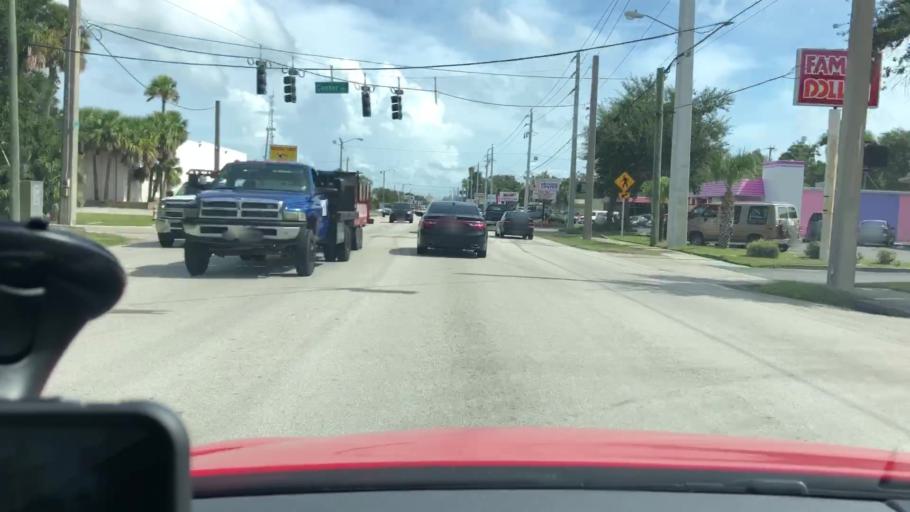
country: US
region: Florida
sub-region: Volusia County
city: Holly Hill
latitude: 29.2229
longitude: -81.0399
